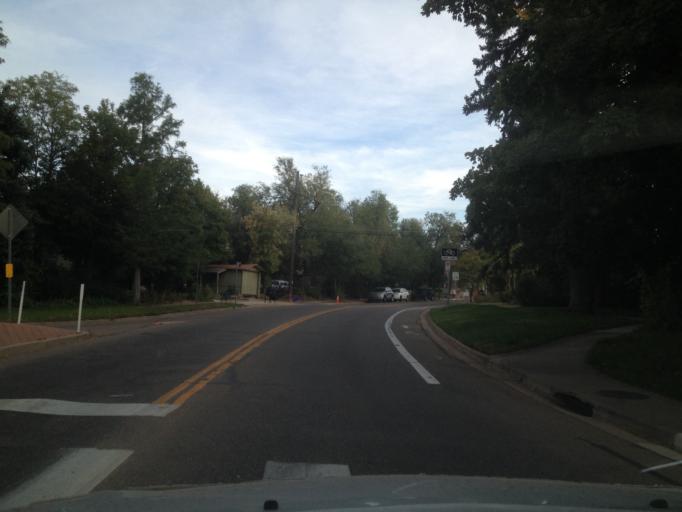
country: US
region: Colorado
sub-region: Boulder County
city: Boulder
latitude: 40.0104
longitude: -105.2823
